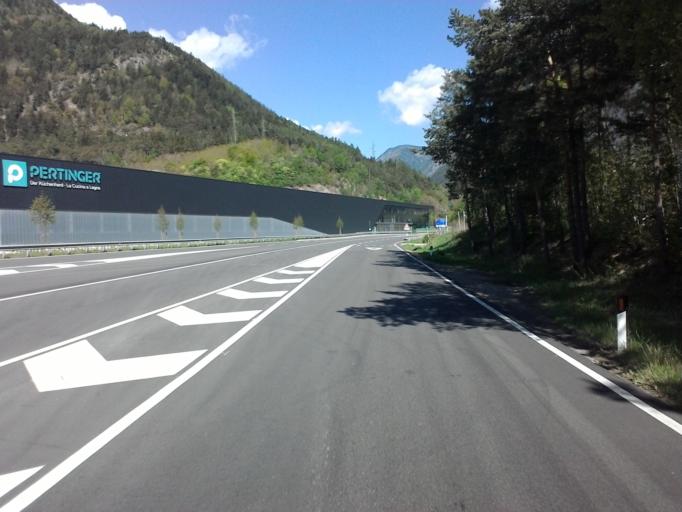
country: IT
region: Trentino-Alto Adige
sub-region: Bolzano
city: Naz-Sciaves - Natz-Schabs
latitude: 46.7671
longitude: 11.6409
